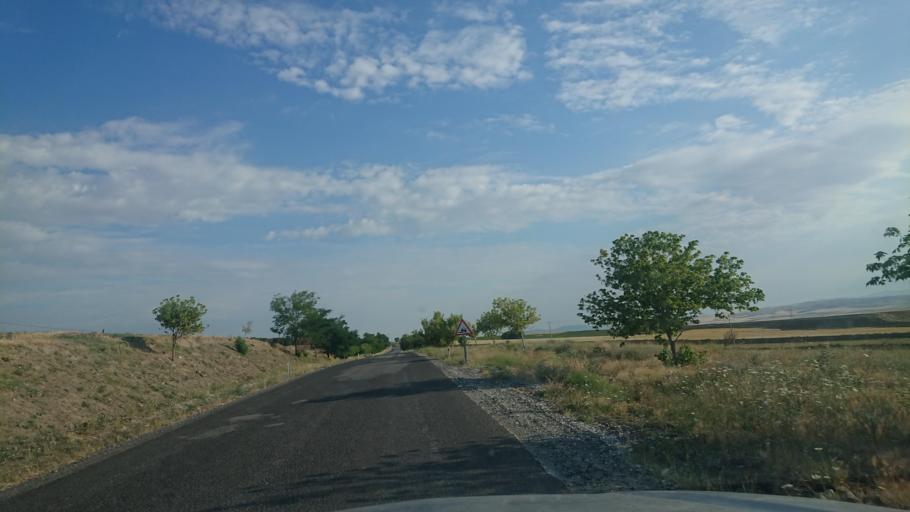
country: TR
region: Aksaray
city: Ortakoy
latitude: 38.8014
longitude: 34.0632
